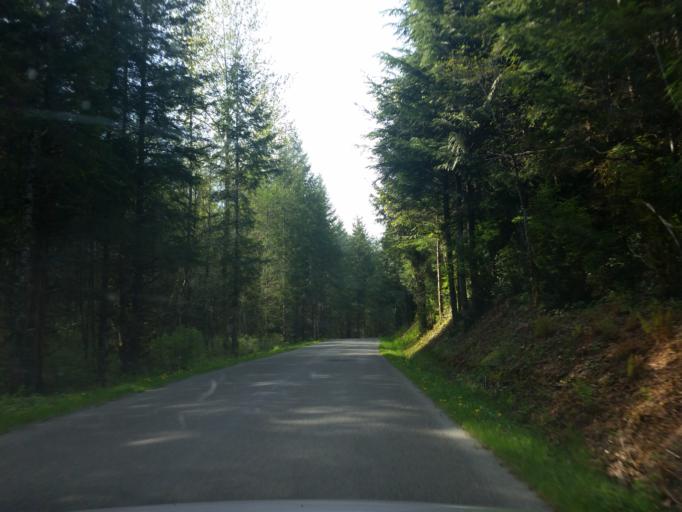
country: US
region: Washington
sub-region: Snohomish County
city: Woods Creek
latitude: 47.9840
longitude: -121.8966
